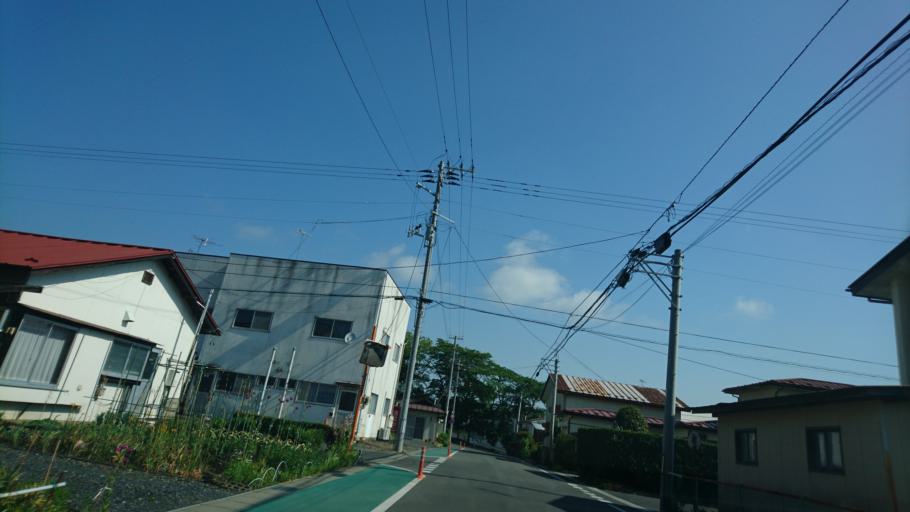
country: JP
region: Iwate
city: Ichinoseki
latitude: 38.9268
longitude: 141.1100
